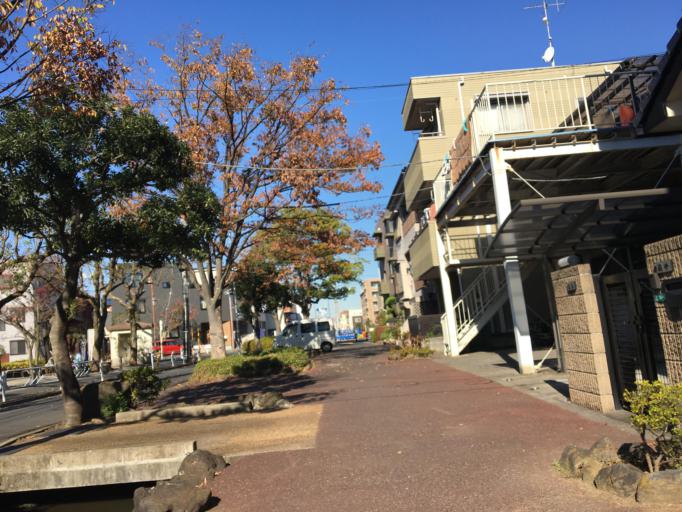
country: JP
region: Tokyo
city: Urayasu
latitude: 35.6876
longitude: 139.8941
